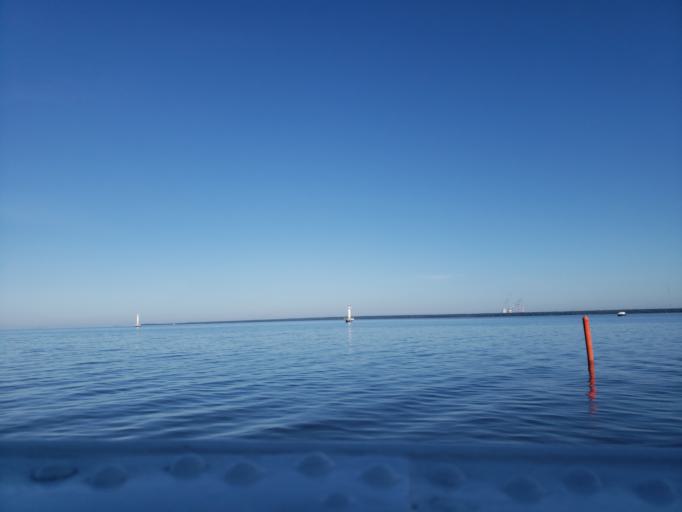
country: RU
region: St.-Petersburg
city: Lakhtinskiy
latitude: 59.9499
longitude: 30.1311
